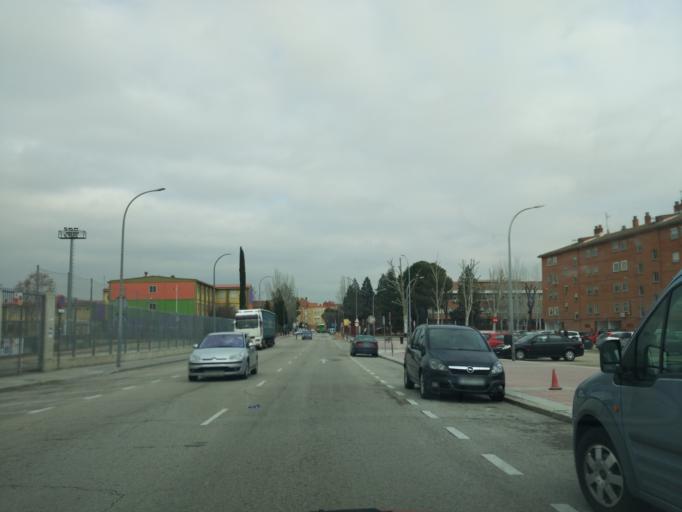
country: ES
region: Madrid
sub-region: Provincia de Madrid
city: Torrejon de Ardoz
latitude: 40.4614
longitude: -3.4894
